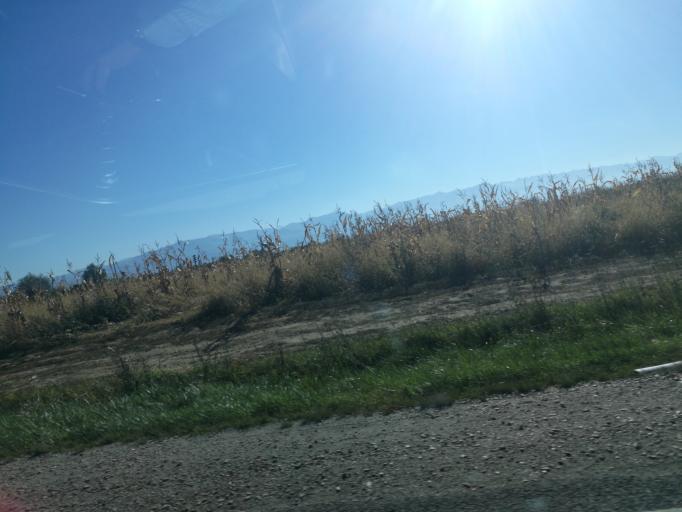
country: RO
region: Brasov
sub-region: Comuna Mandra
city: Mandra
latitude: 45.8325
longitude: 25.0135
